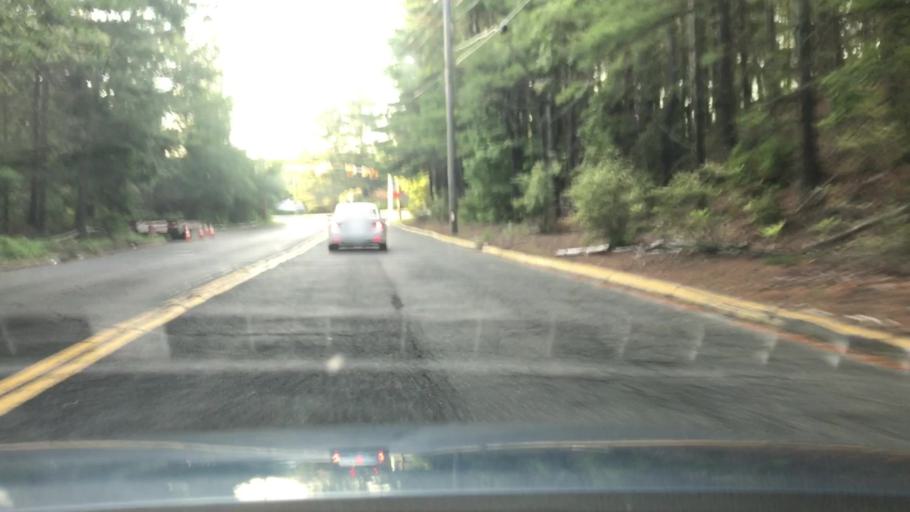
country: US
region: Massachusetts
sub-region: Worcester County
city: Northborough
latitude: 42.3345
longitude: -71.6017
